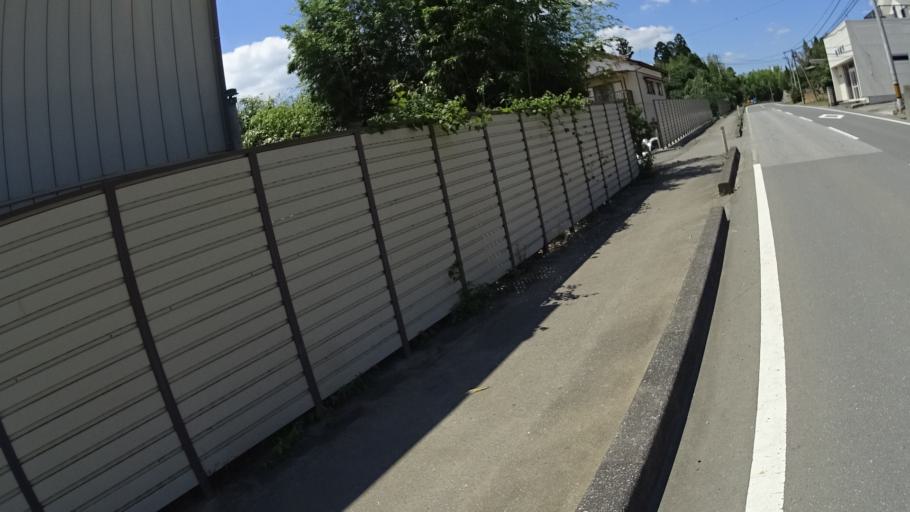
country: JP
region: Iwate
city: Ofunato
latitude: 38.8414
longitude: 141.6188
